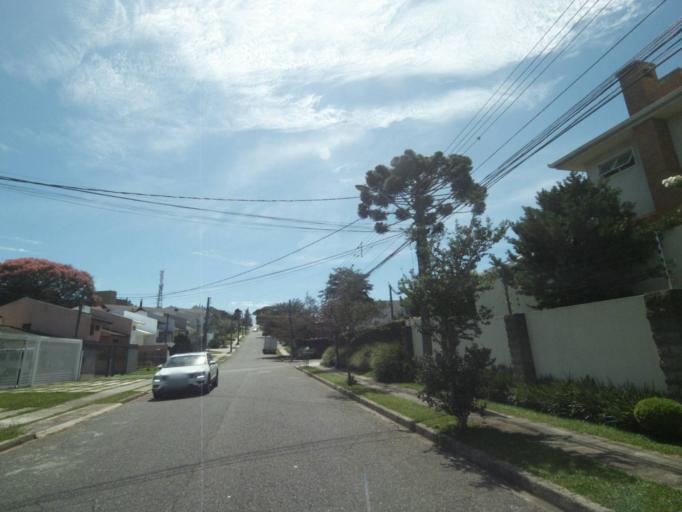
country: BR
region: Parana
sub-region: Curitiba
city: Curitiba
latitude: -25.4623
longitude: -49.2409
